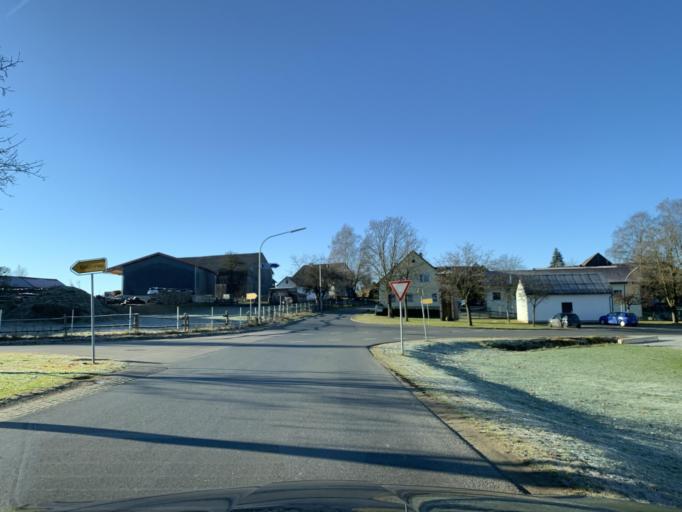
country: DE
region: Bavaria
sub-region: Upper Palatinate
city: Oberviechtach
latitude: 49.4549
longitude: 12.4474
